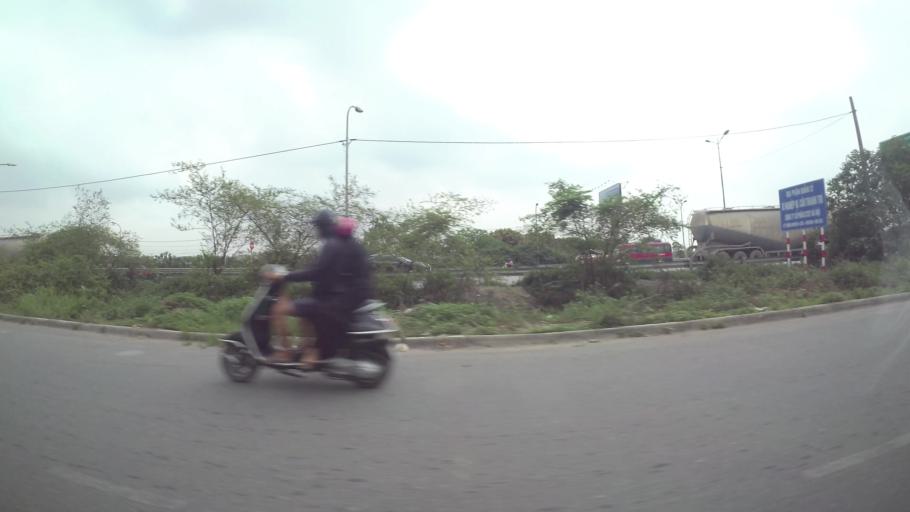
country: VN
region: Ha Noi
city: Trau Quy
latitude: 21.0332
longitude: 105.9327
